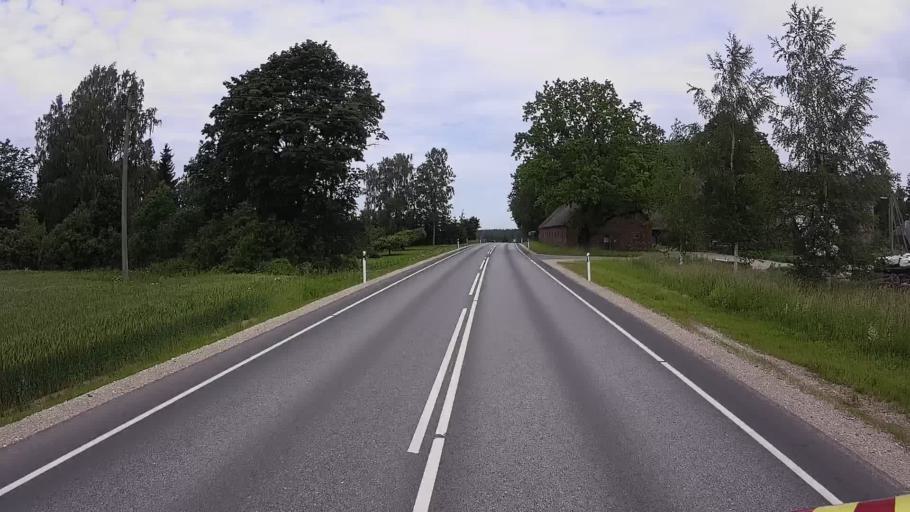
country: EE
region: Viljandimaa
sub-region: Viljandi linn
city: Viljandi
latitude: 58.2712
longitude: 25.5835
